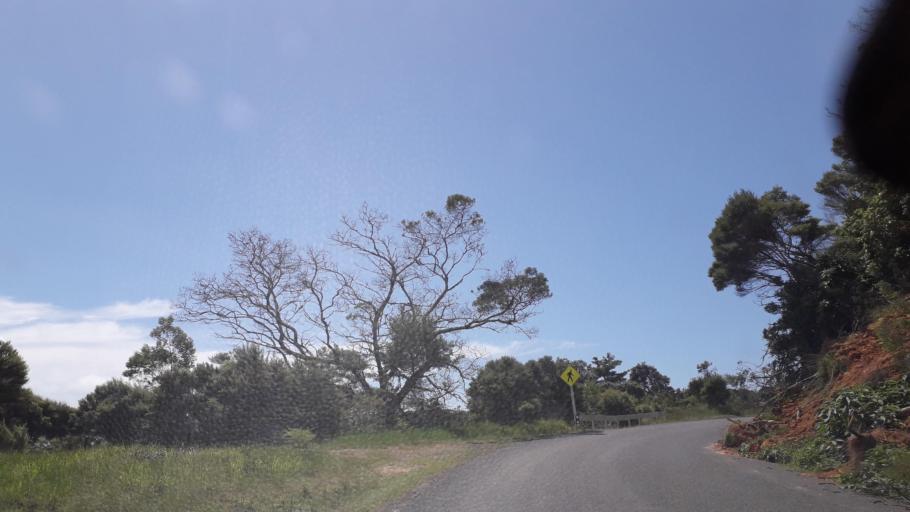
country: NZ
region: Northland
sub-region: Far North District
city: Paihia
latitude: -35.2352
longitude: 174.2604
